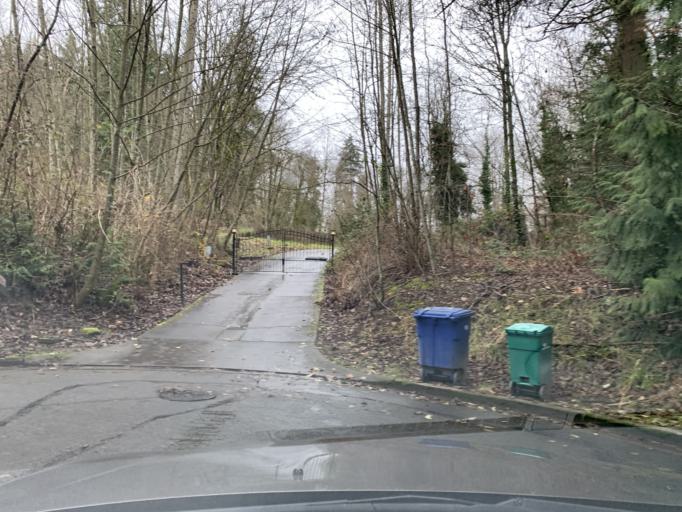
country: US
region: Washington
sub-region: King County
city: Tukwila
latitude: 47.4614
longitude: -122.2706
